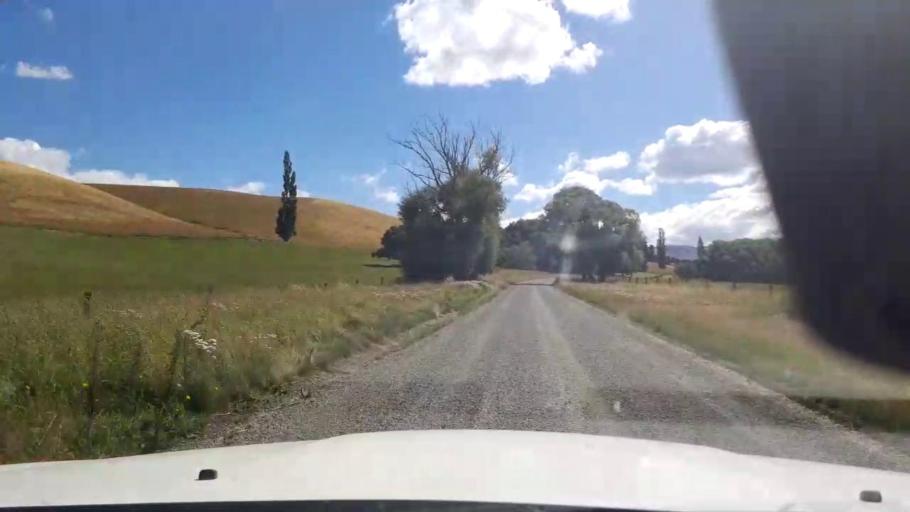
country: NZ
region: Canterbury
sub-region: Timaru District
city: Pleasant Point
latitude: -44.3177
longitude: 170.9435
